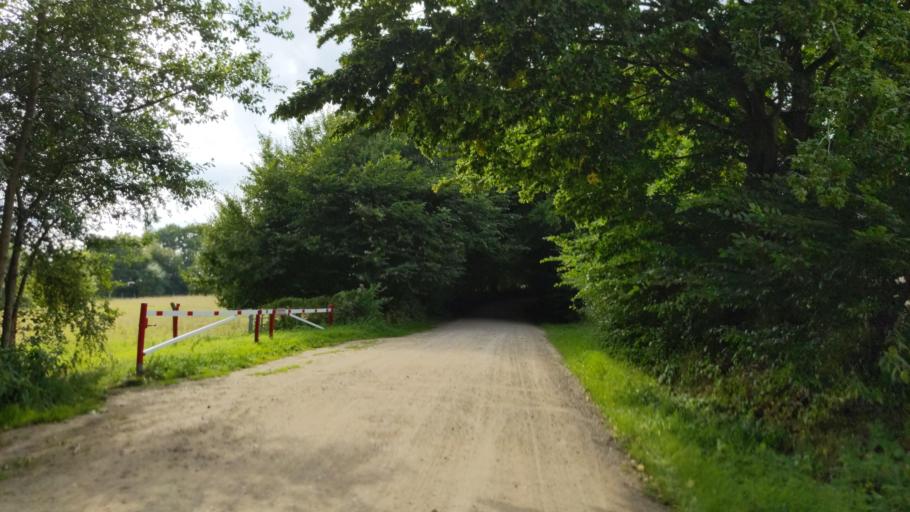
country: DE
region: Schleswig-Holstein
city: Eutin
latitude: 54.1598
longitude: 10.6507
